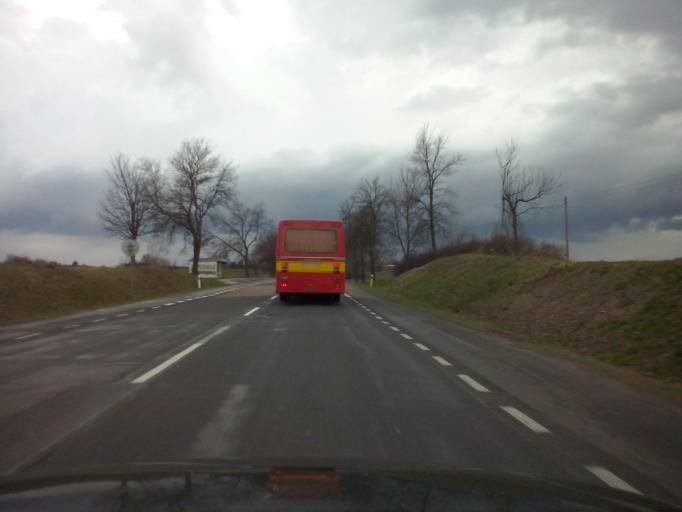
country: PL
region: Lublin Voivodeship
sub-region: Powiat chelmski
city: Rejowiec Fabryczny
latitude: 51.1735
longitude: 23.2757
